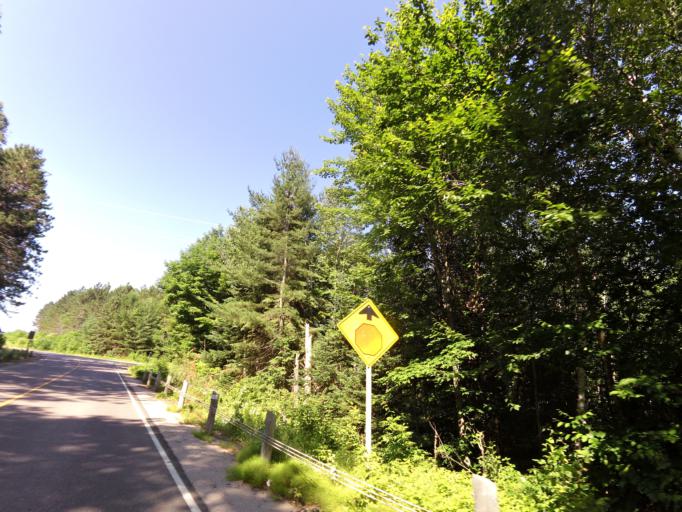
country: CA
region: Ontario
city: Deep River
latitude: 46.1747
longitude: -77.6927
